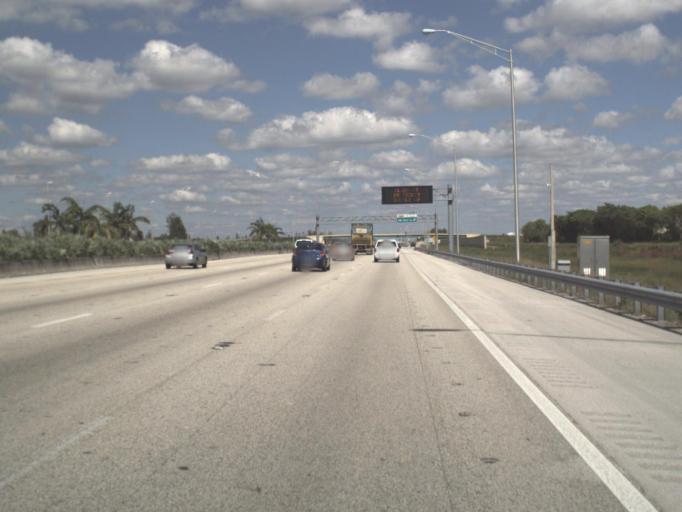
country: US
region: Florida
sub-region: Miami-Dade County
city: Doral
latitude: 25.8322
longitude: -80.3867
